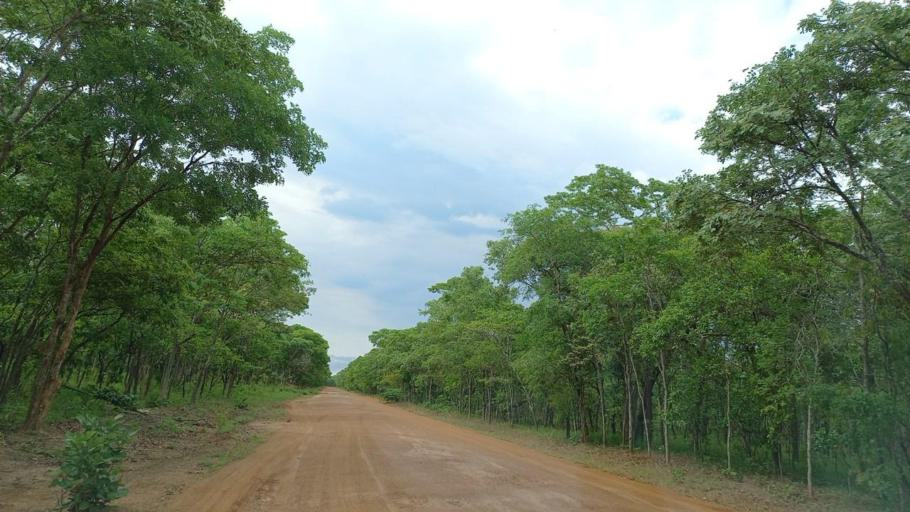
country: ZM
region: North-Western
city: Kalengwa
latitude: -13.3843
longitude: 25.0715
